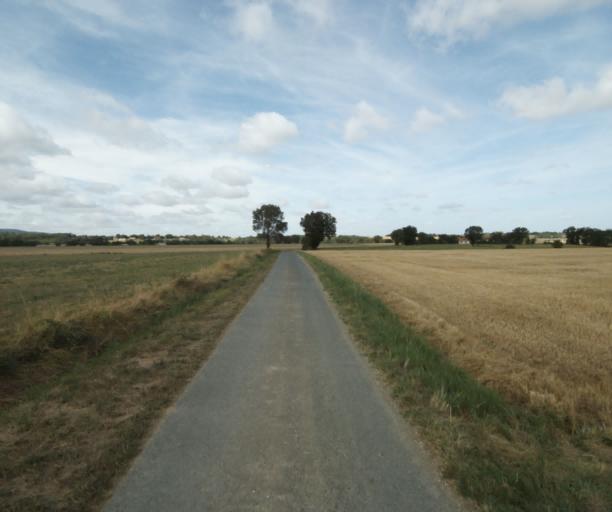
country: FR
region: Midi-Pyrenees
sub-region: Departement du Tarn
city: Soreze
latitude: 43.4772
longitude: 2.0918
